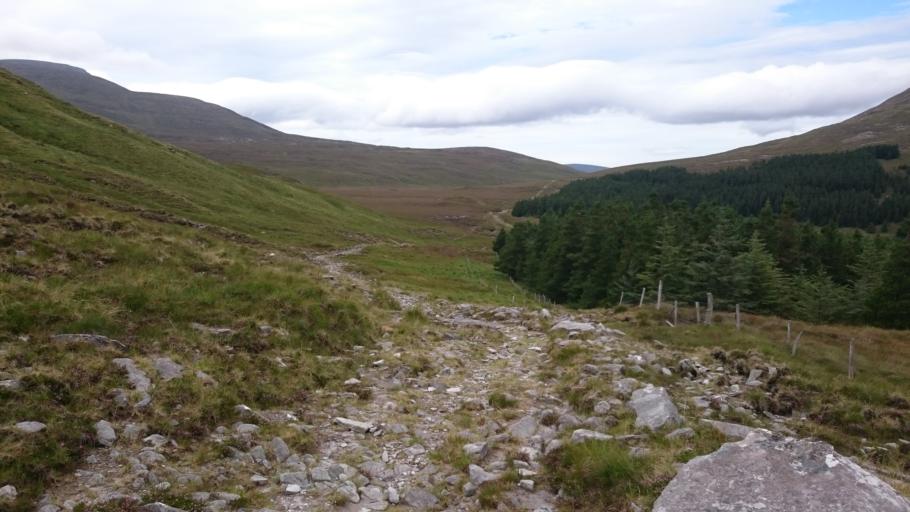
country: IE
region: Connaught
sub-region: Maigh Eo
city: Westport
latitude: 54.0017
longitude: -9.6104
